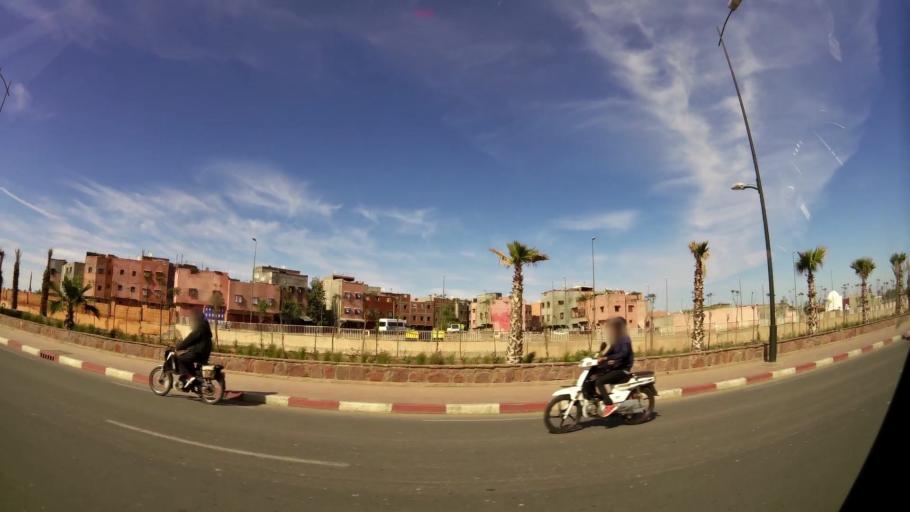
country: MA
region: Marrakech-Tensift-Al Haouz
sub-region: Marrakech
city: Marrakesh
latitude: 31.6335
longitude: -7.9777
